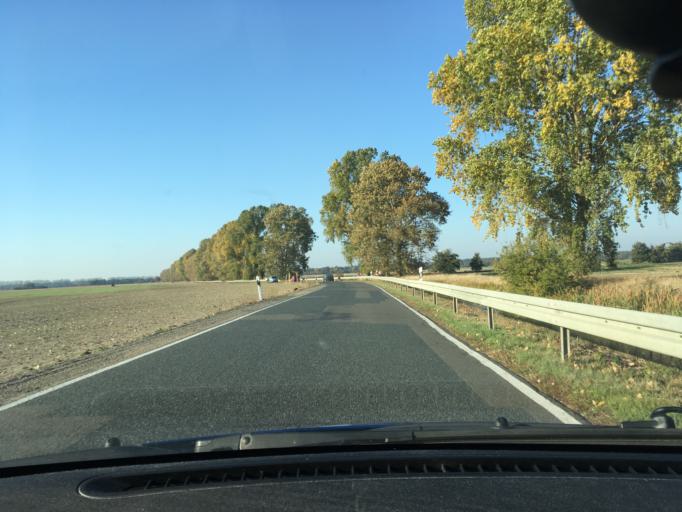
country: DE
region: Mecklenburg-Vorpommern
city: Domitz
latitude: 53.1496
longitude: 11.2580
